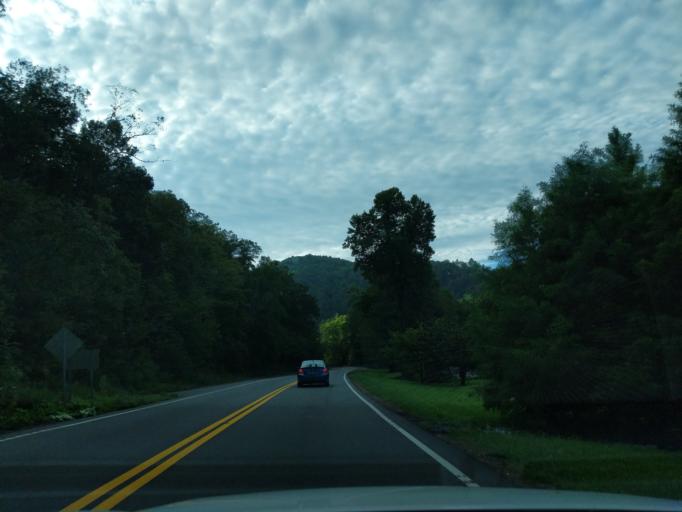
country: US
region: Tennessee
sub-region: Polk County
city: Benton
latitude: 35.0973
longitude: -84.5486
